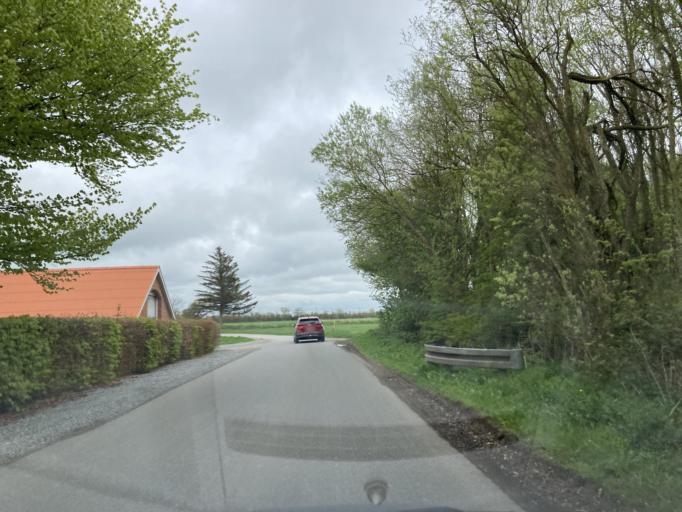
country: DK
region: North Denmark
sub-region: Thisted Kommune
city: Hurup
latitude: 56.8140
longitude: 8.3274
